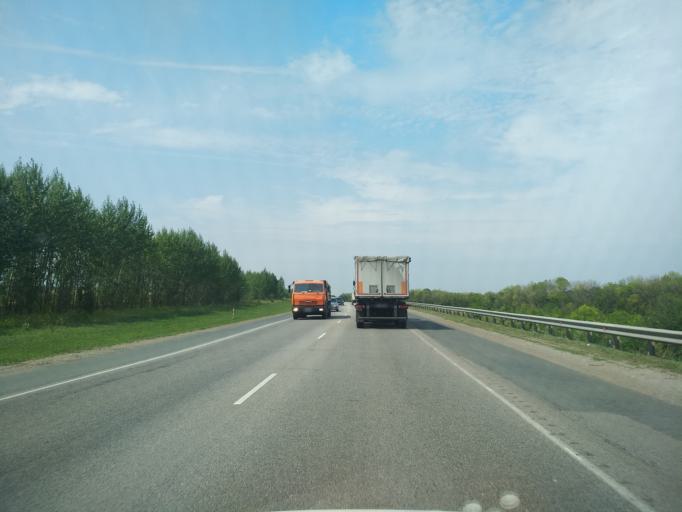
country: RU
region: Voronezj
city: Novaya Usman'
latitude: 51.7009
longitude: 39.4144
